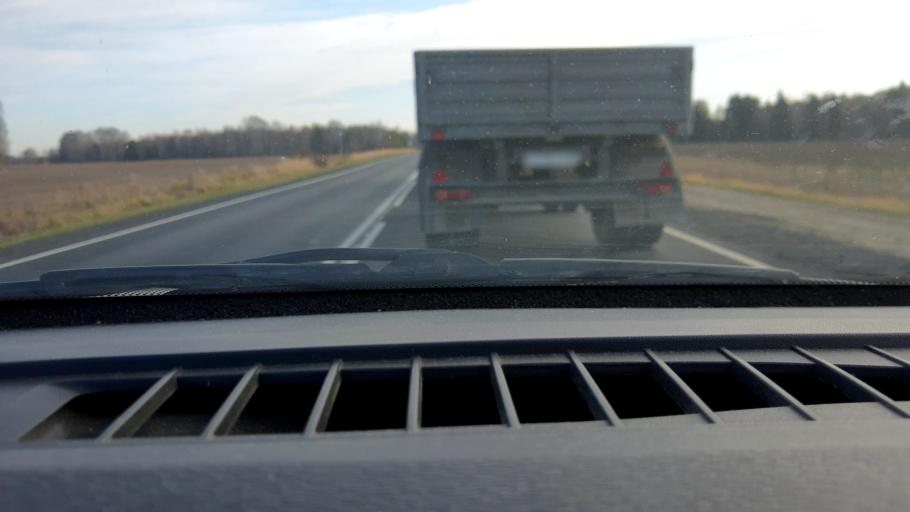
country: RU
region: Nizjnij Novgorod
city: Novaya Balakhna
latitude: 56.5963
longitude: 43.6453
